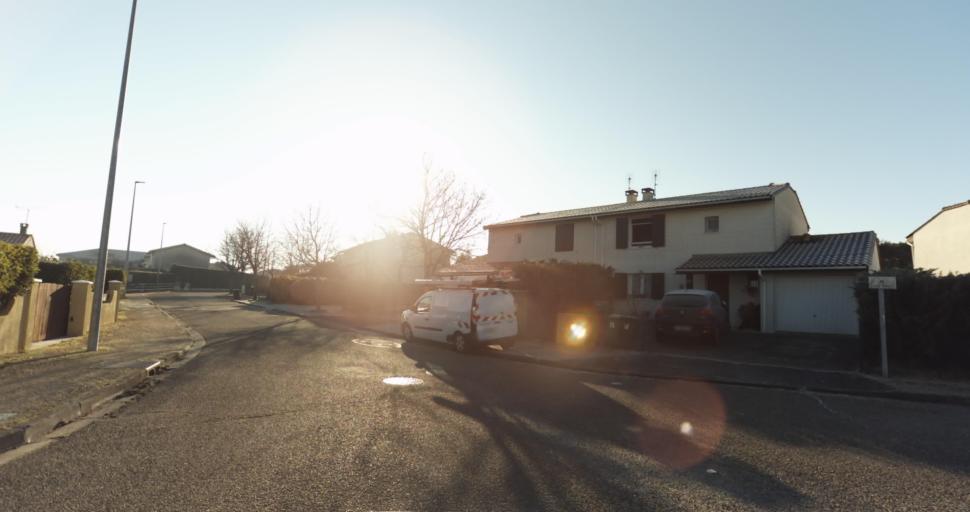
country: FR
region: Aquitaine
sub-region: Departement de la Gironde
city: Carbon-Blanc
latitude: 44.8979
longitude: -0.5035
